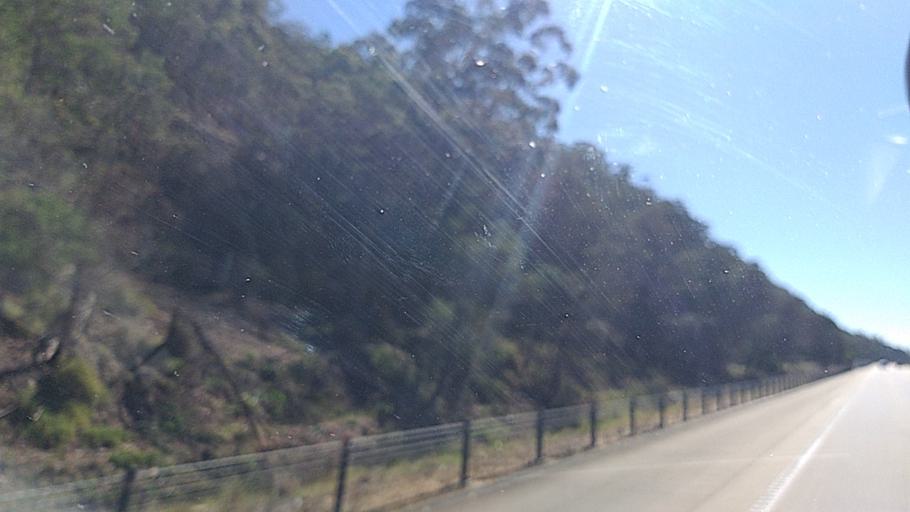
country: AU
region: New South Wales
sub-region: Yass Valley
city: Gundaroo
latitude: -35.0553
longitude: 149.3750
